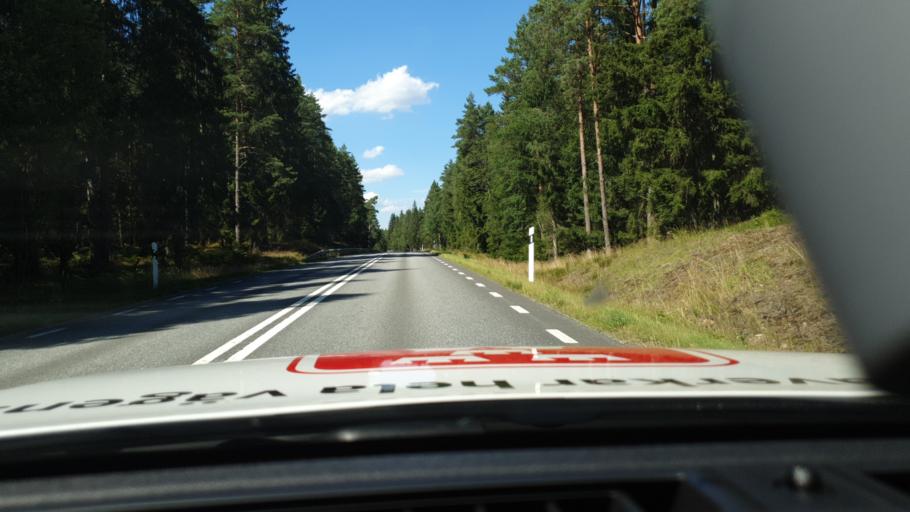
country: SE
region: Joenkoeping
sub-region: Savsjo Kommun
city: Vrigstad
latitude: 57.3785
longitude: 14.4041
